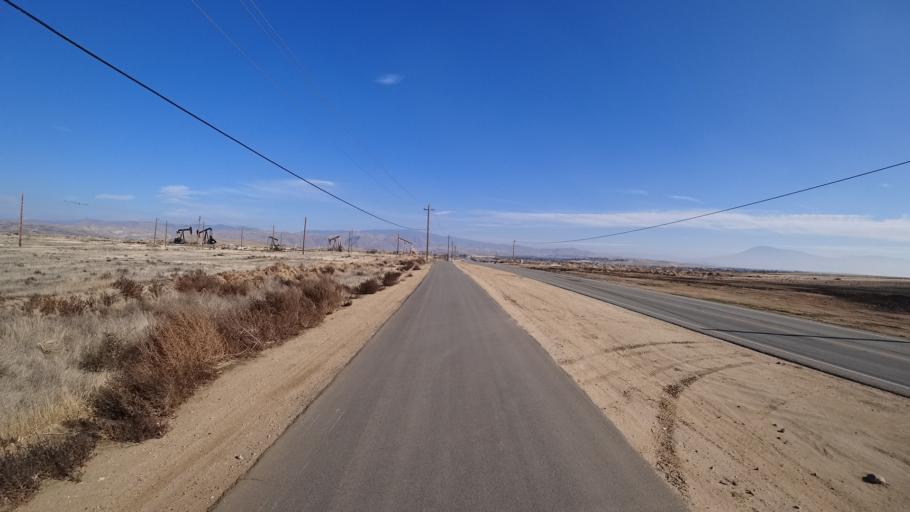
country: US
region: California
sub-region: Kern County
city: Oildale
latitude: 35.4128
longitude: -118.9072
